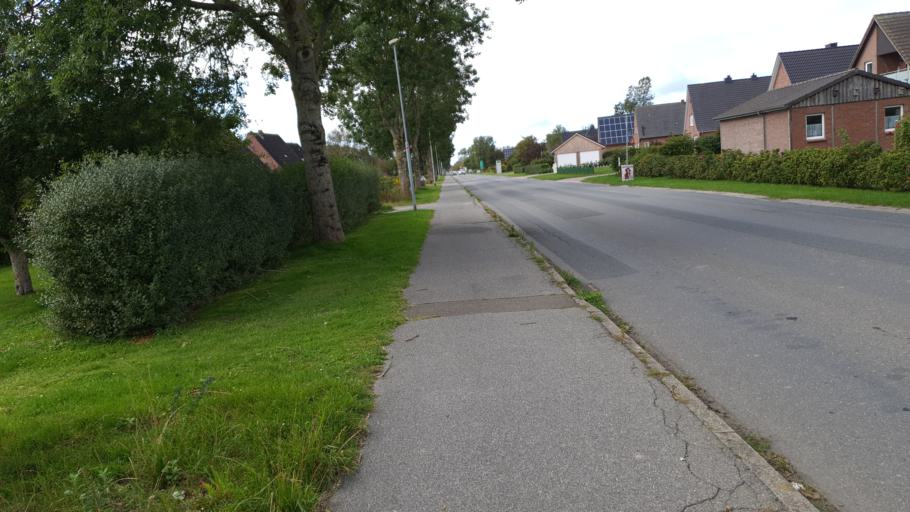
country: DE
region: Schleswig-Holstein
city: Elisabeth-Sophien-Koog
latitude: 54.4887
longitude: 8.8824
